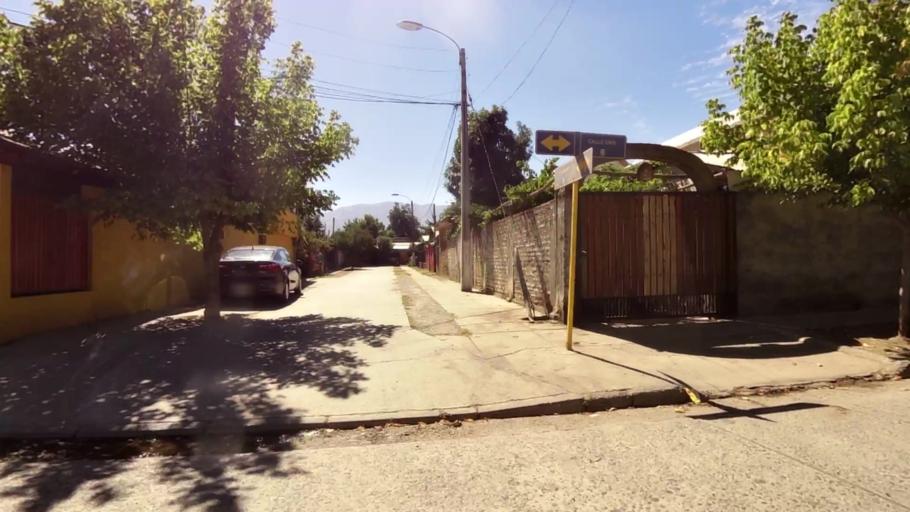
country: CL
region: O'Higgins
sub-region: Provincia de Cachapoal
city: Graneros
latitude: -33.9729
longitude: -70.7104
